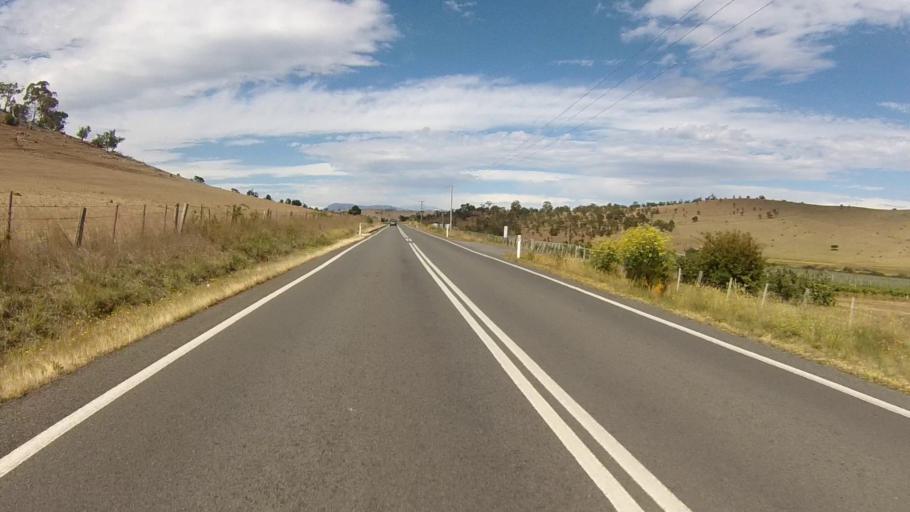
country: AU
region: Tasmania
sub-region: Brighton
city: Old Beach
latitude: -42.6782
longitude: 147.3558
